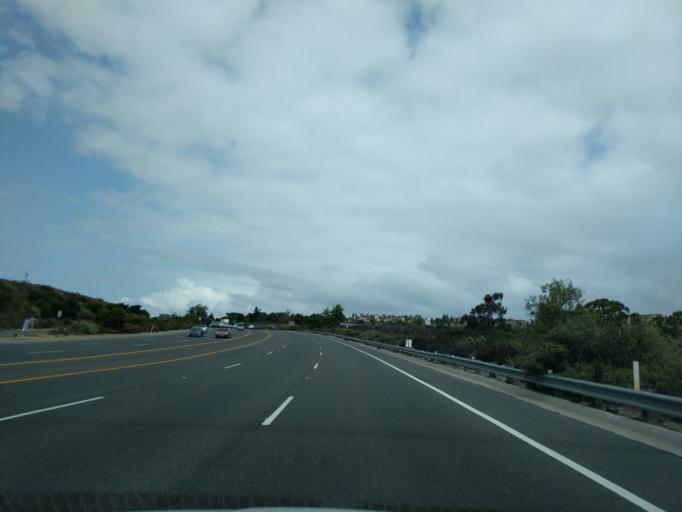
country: US
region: California
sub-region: Orange County
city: San Joaquin Hills
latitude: 33.5762
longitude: -117.8400
